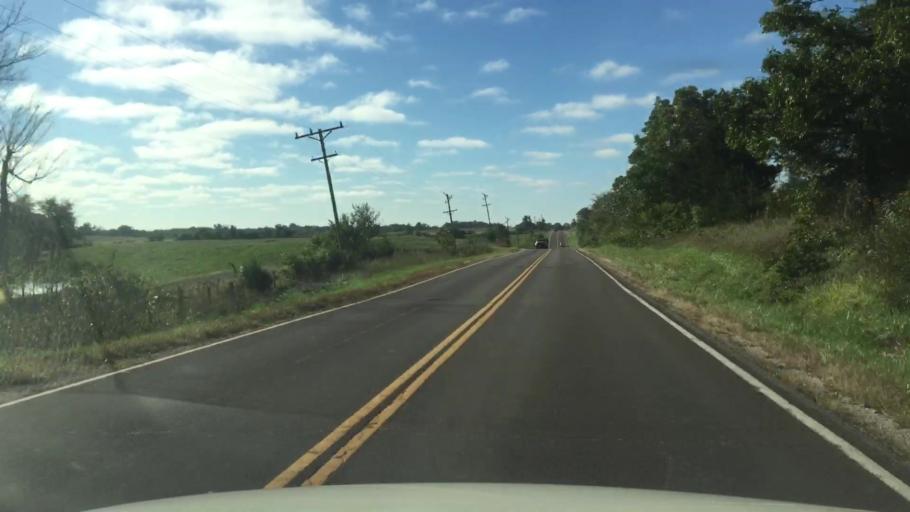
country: US
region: Missouri
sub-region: Howard County
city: New Franklin
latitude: 39.0810
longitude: -92.7455
